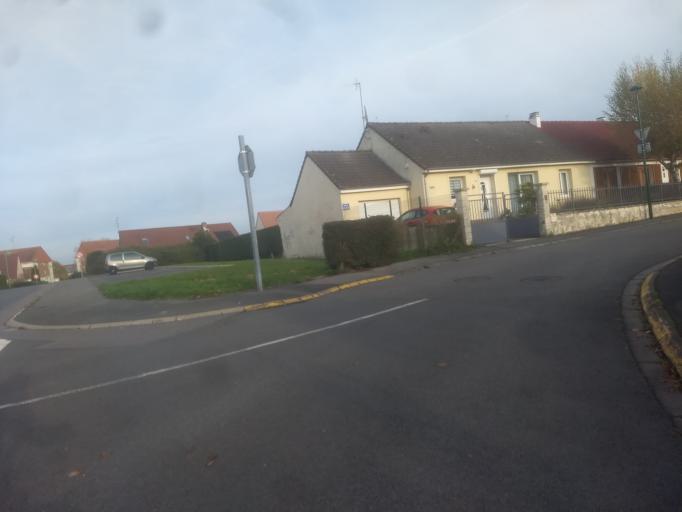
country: FR
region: Nord-Pas-de-Calais
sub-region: Departement du Pas-de-Calais
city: Achicourt
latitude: 50.2713
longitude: 2.7762
